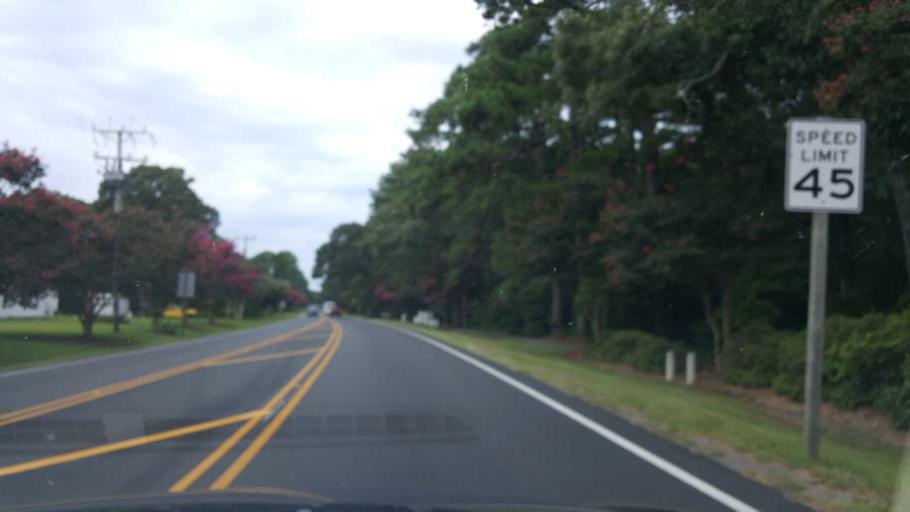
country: US
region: North Carolina
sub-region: Dare County
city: Manteo
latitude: 35.9325
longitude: -75.6923
